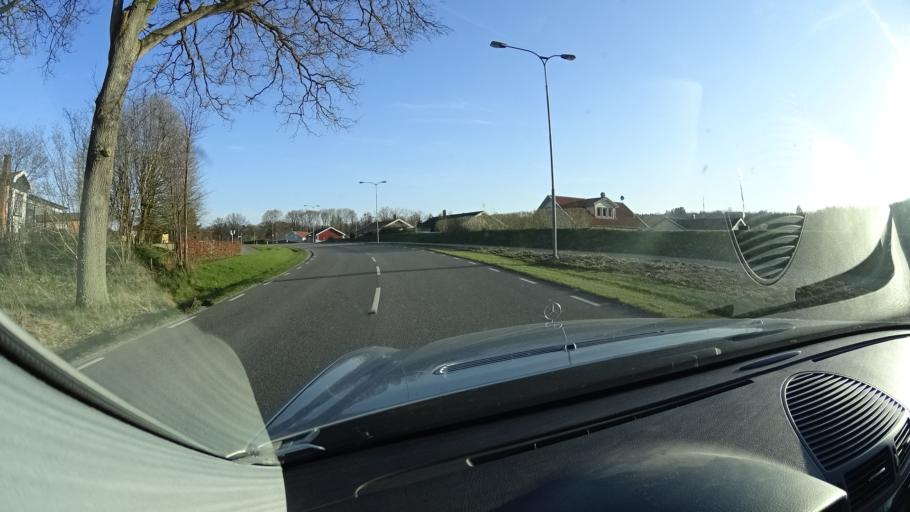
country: SE
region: Skane
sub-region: Hoors Kommun
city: Satofta
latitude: 55.9168
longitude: 13.5463
